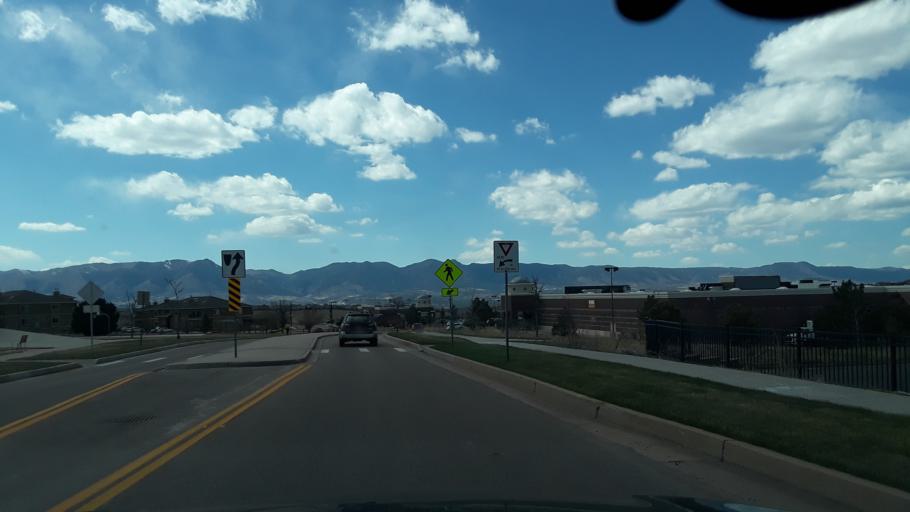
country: US
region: Colorado
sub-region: El Paso County
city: Black Forest
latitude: 38.9634
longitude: -104.7538
